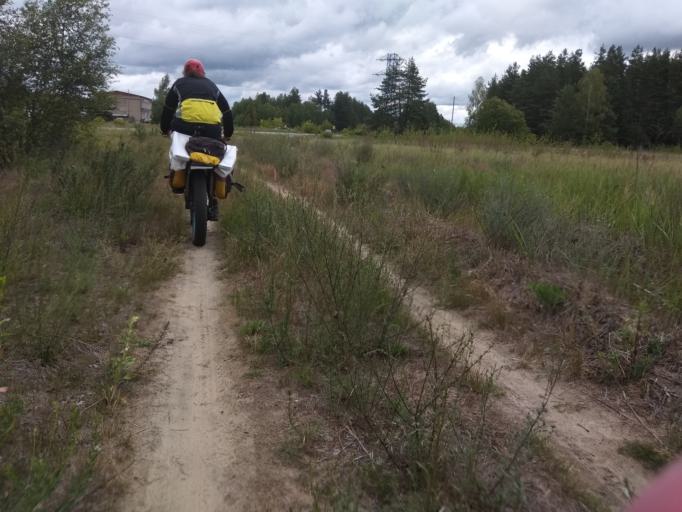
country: RU
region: Moskovskaya
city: Kerva
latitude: 55.5778
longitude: 39.6872
